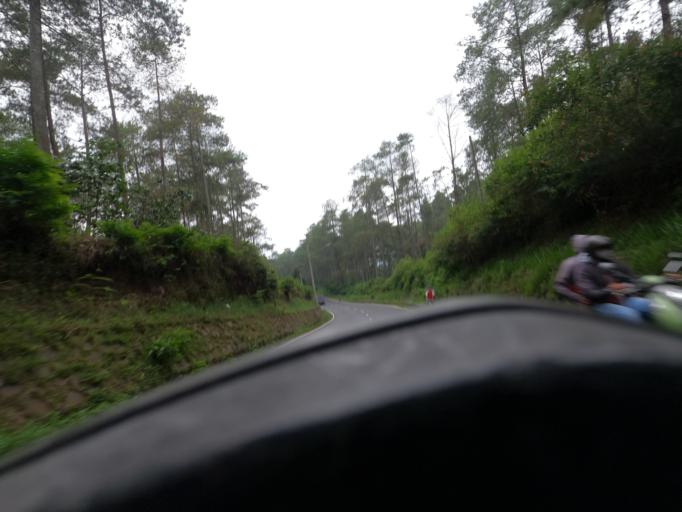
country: ID
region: West Java
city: Lembang
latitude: -6.7763
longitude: 107.6395
